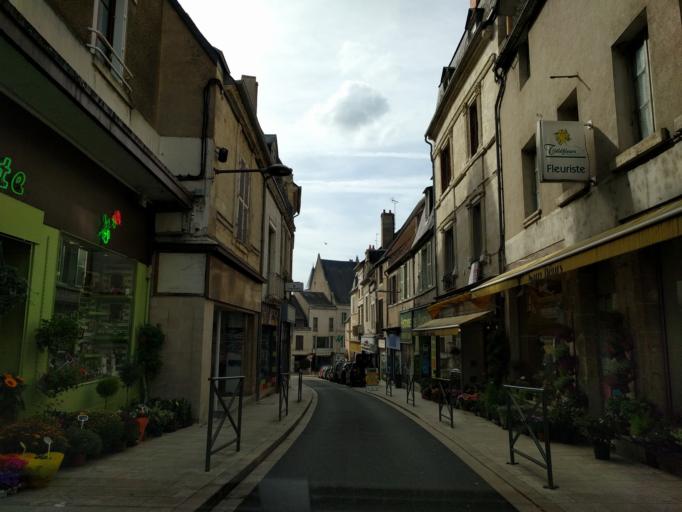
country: FR
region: Bourgogne
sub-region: Departement de la Nievre
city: La Charite-sur-Loire
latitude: 47.1773
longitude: 3.0175
